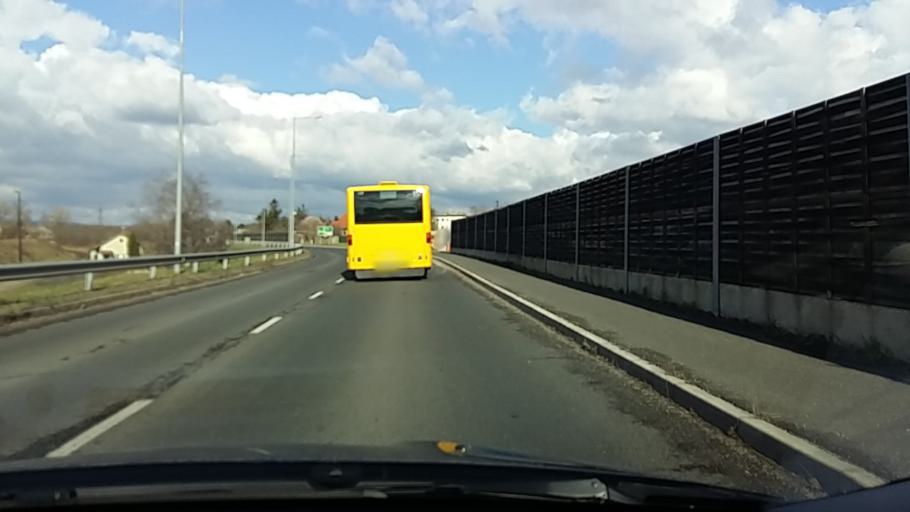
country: HU
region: Veszprem
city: Tapolca
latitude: 46.8809
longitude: 17.4256
